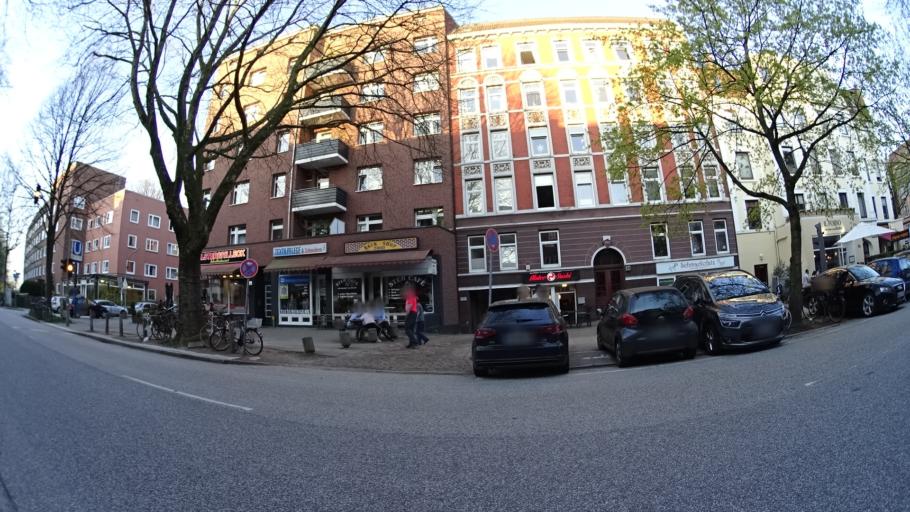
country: DE
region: Hamburg
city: Winterhude
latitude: 53.5995
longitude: 9.9968
